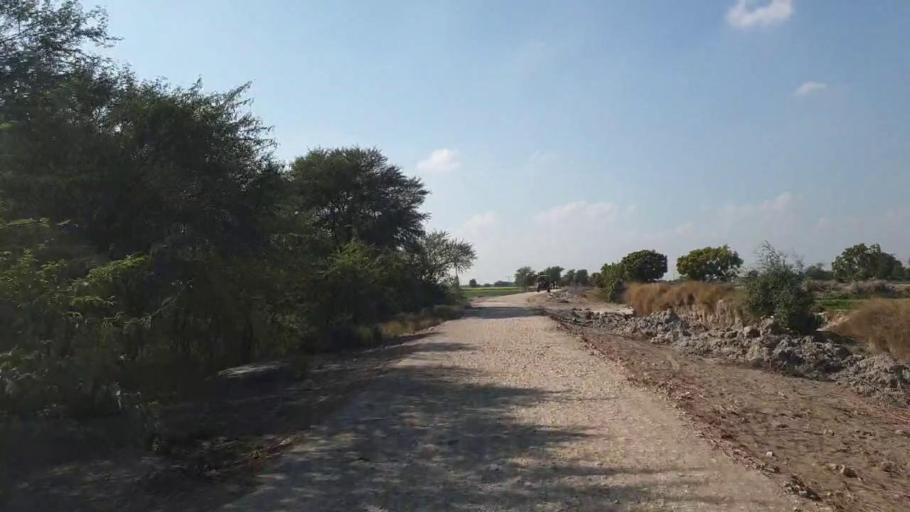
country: PK
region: Sindh
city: Shahpur Chakar
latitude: 26.0789
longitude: 68.5763
